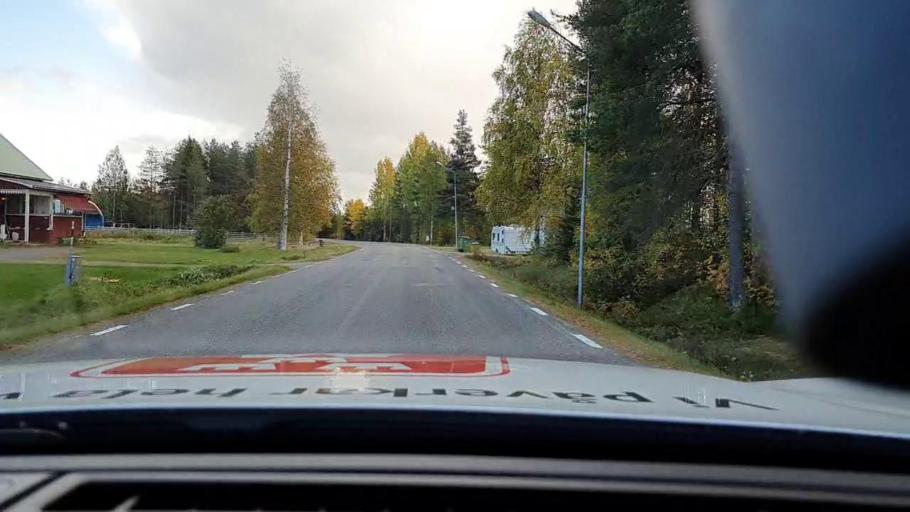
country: SE
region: Vaesterbotten
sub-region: Skelleftea Kommun
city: Langsele
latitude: 64.9477
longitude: 19.9345
